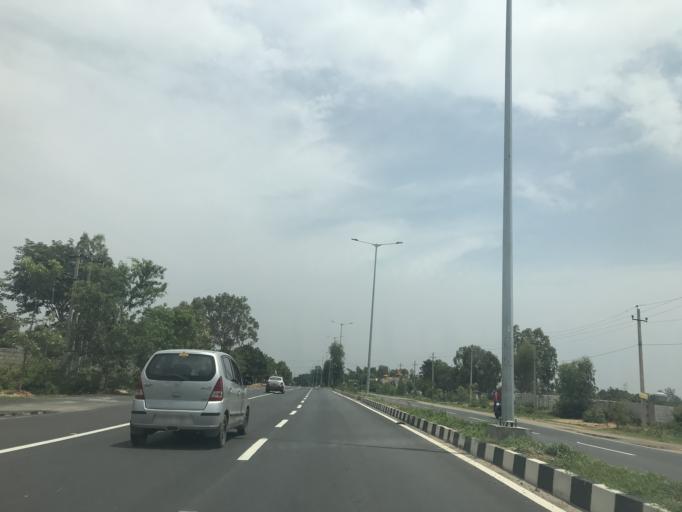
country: IN
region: Karnataka
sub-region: Bangalore Urban
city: Yelahanka
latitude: 13.1522
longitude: 77.6769
